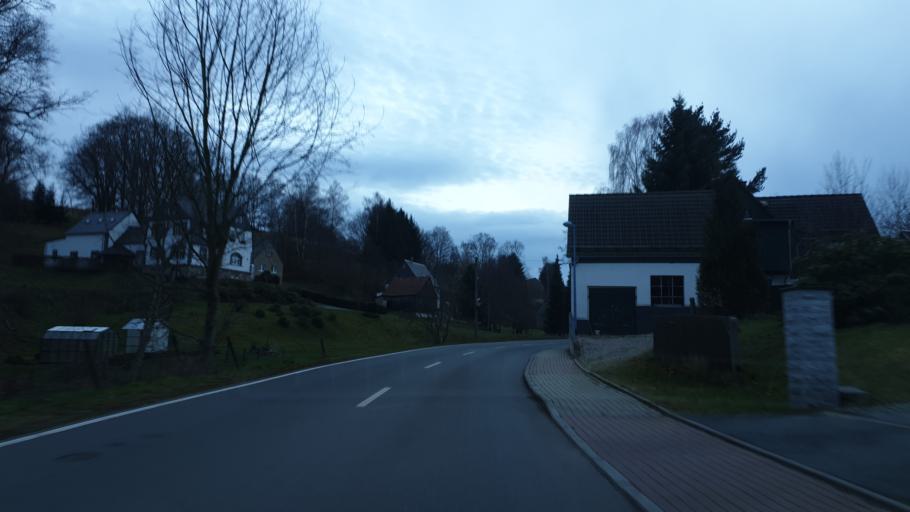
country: DE
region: Saxony
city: Oelsnitz
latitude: 50.7096
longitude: 12.6844
